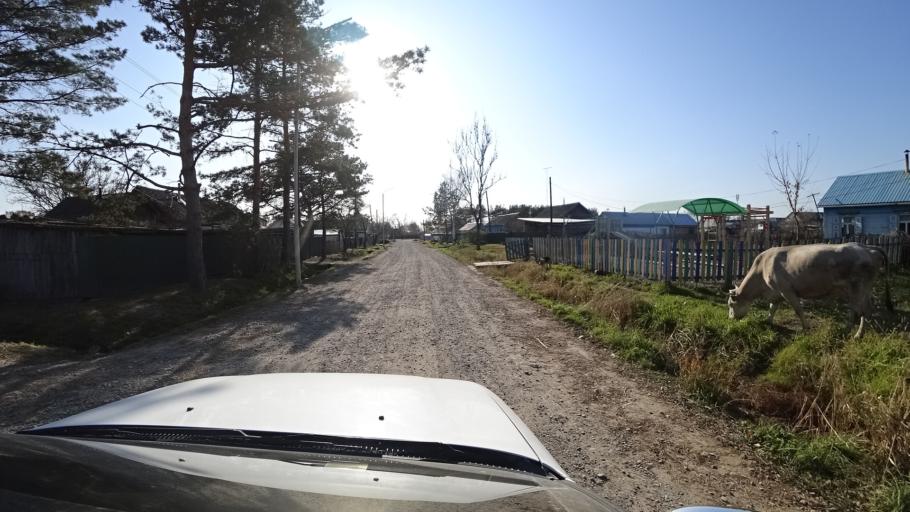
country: RU
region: Primorskiy
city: Dal'nerechensk
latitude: 45.9237
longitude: 133.7491
